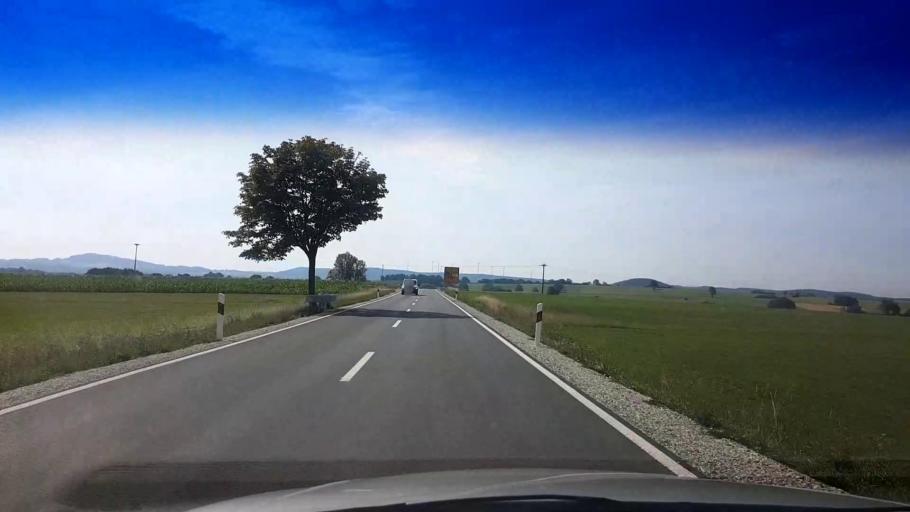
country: DE
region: Bavaria
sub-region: Upper Franconia
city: Mistelgau
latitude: 49.9330
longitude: 11.4730
